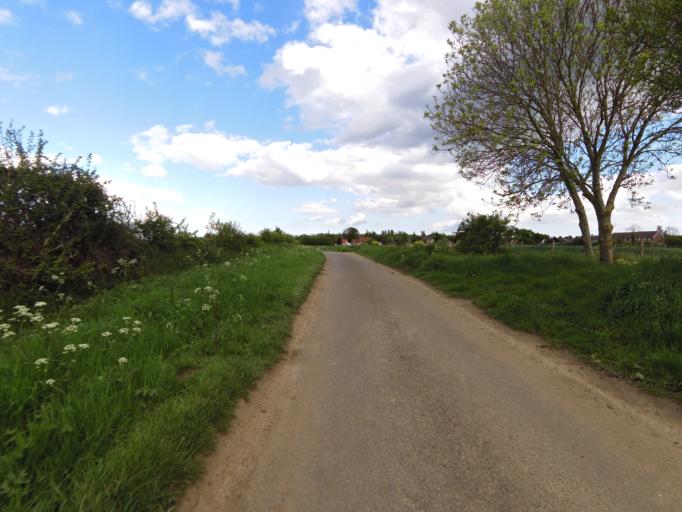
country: GB
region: England
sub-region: Suffolk
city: Elmswell
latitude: 52.2051
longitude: 0.9426
